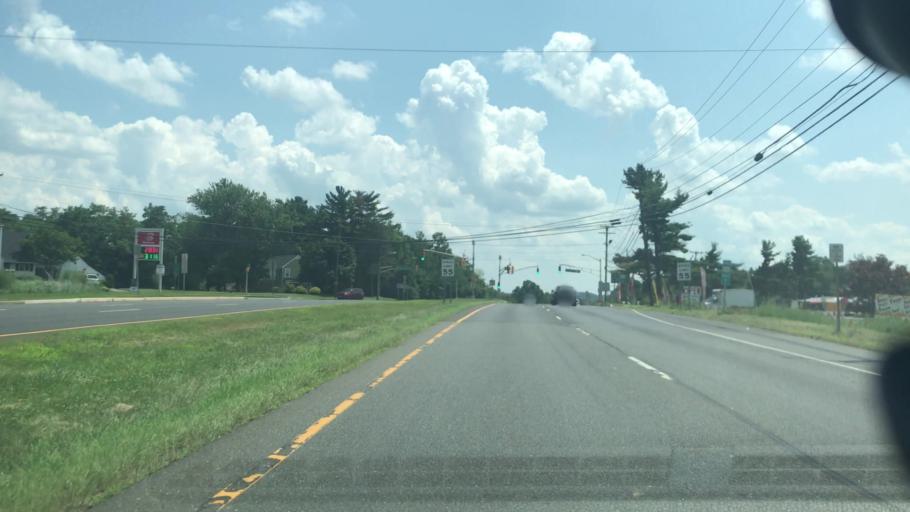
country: US
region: New Jersey
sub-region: Hunterdon County
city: Flemington
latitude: 40.4415
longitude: -74.8580
